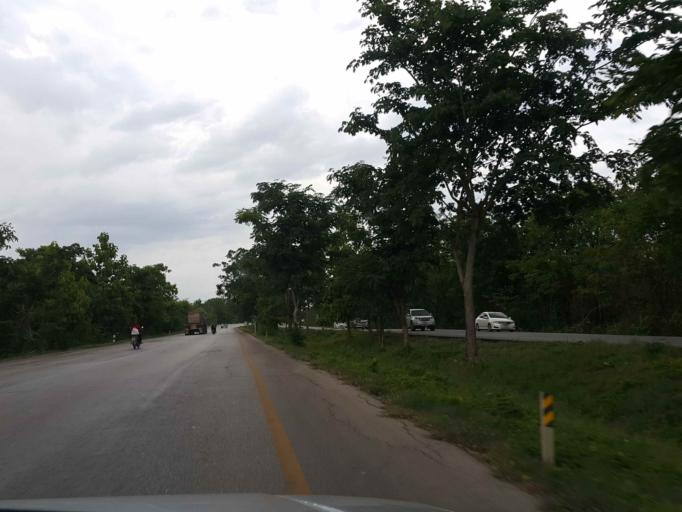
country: TH
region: Lampang
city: Sop Prap
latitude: 17.9775
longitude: 99.3558
